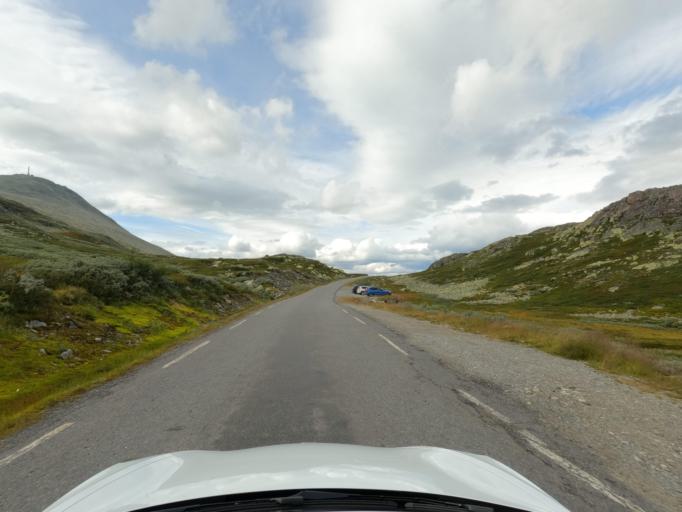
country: NO
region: Telemark
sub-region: Tinn
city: Rjukan
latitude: 59.8418
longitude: 8.7047
